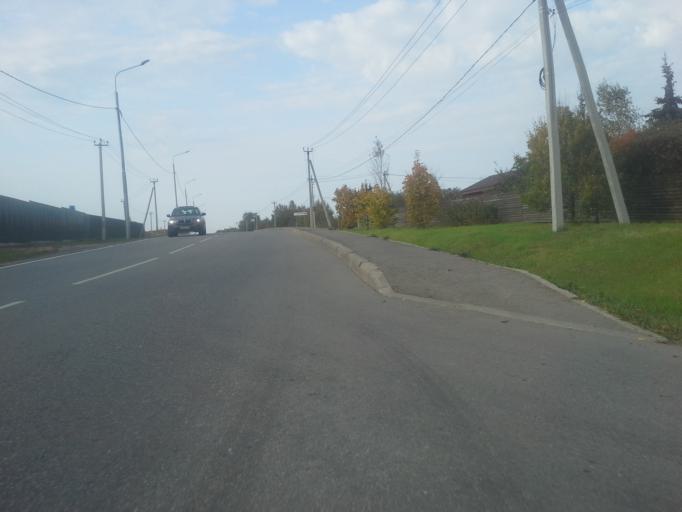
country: RU
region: Moskovskaya
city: Selyatino
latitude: 55.4303
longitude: 36.9614
